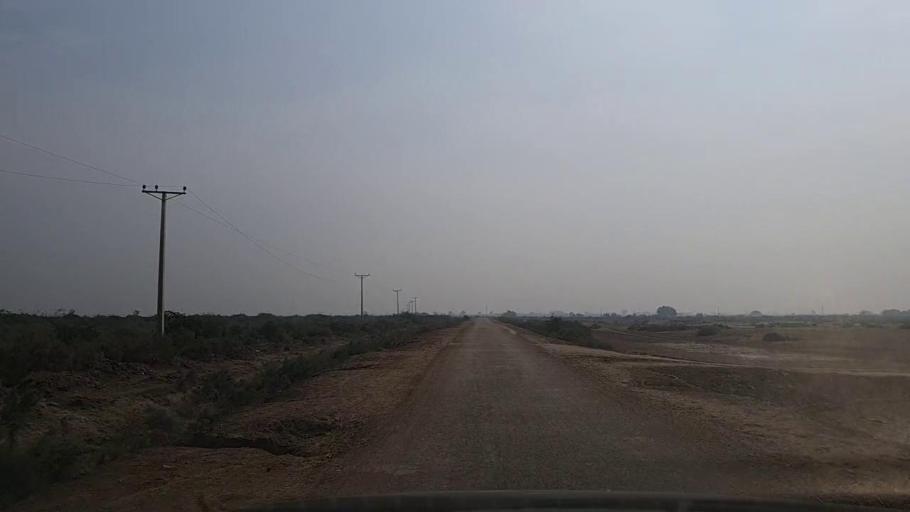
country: PK
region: Sindh
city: Mirpur Sakro
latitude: 24.3887
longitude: 67.7522
